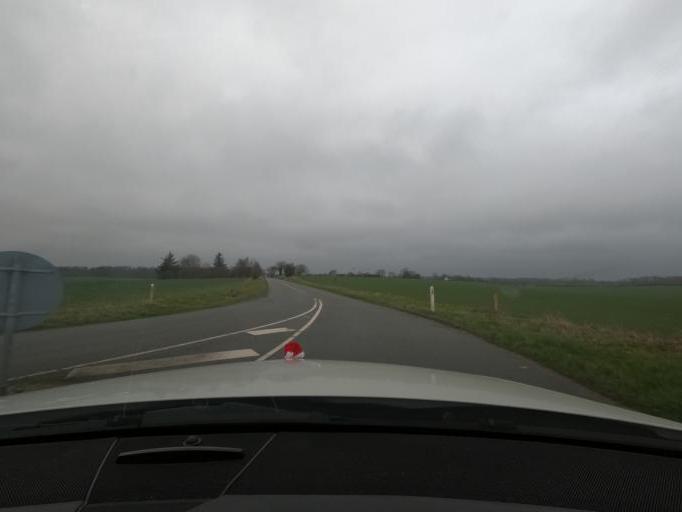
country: DK
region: South Denmark
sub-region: Haderslev Kommune
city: Starup
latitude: 55.2120
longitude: 9.6365
